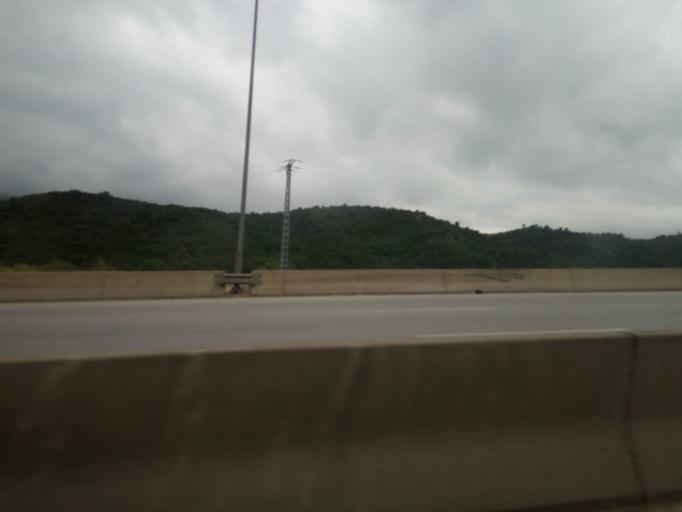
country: DZ
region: Bouira
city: Lakhdaria
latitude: 36.5777
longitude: 3.5509
